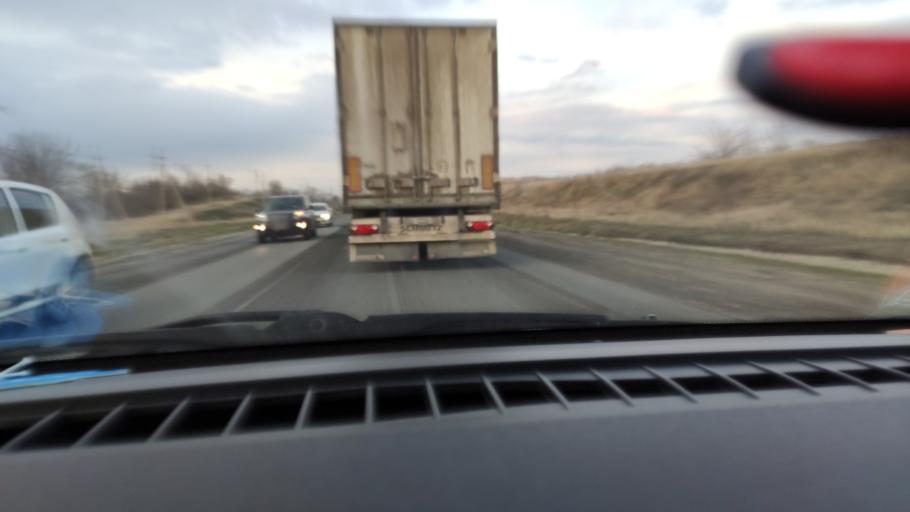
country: RU
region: Saratov
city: Shumeyka
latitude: 51.7867
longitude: 46.1397
